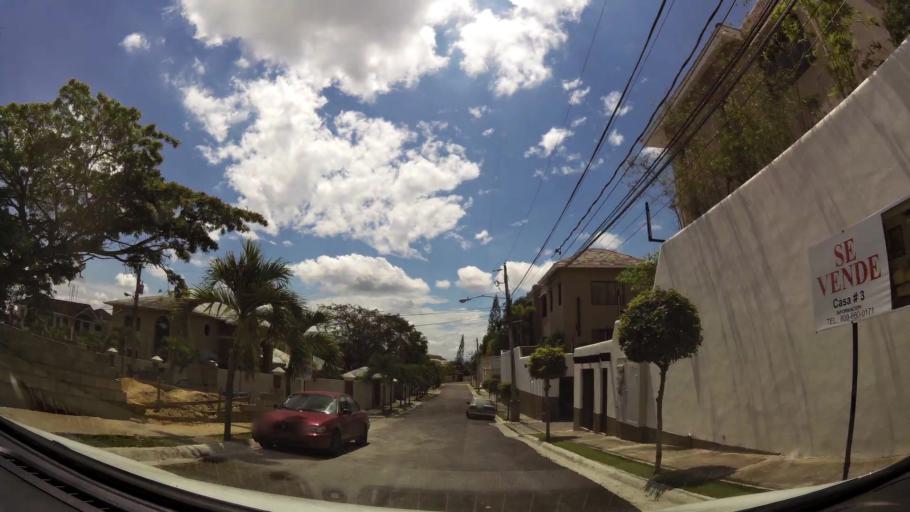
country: DO
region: Santiago
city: Santiago de los Caballeros
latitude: 19.4670
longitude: -70.6763
